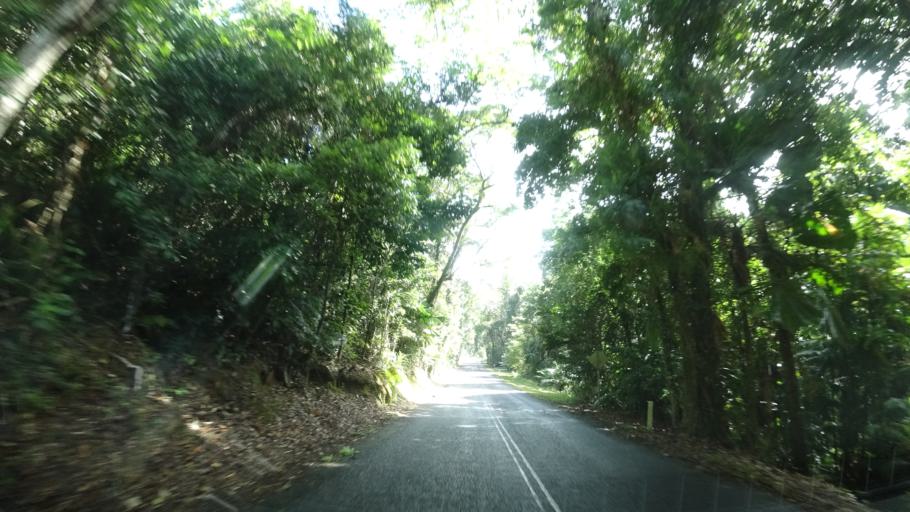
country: AU
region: Queensland
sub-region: Cairns
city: Port Douglas
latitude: -16.2600
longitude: 145.4224
